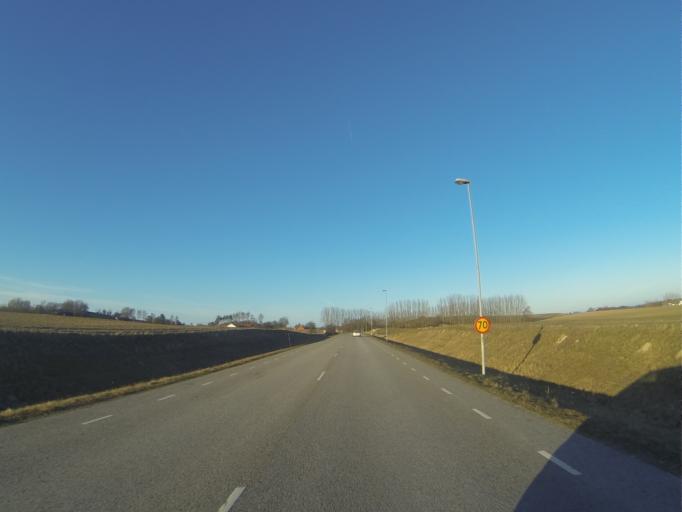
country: SE
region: Skane
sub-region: Malmo
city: Oxie
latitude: 55.5591
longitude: 13.1065
